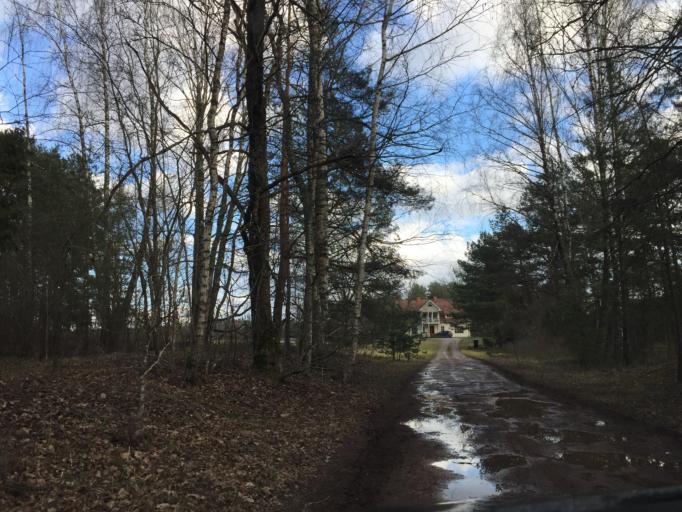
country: LV
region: Adazi
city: Adazi
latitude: 57.0580
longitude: 24.3380
